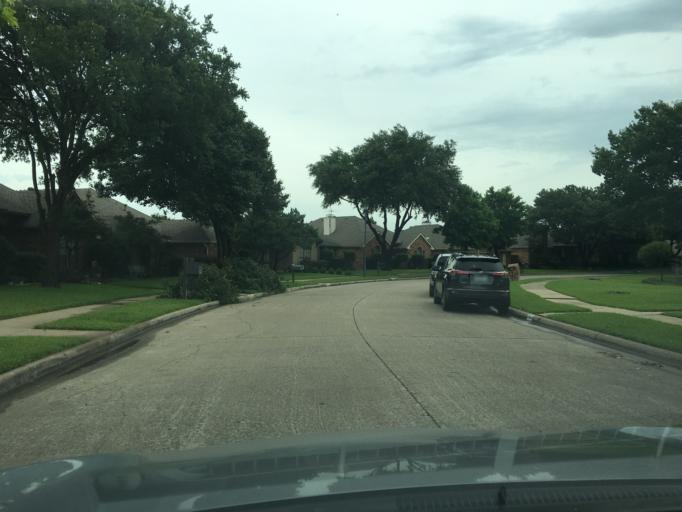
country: US
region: Texas
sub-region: Dallas County
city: Garland
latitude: 32.9414
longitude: -96.6721
